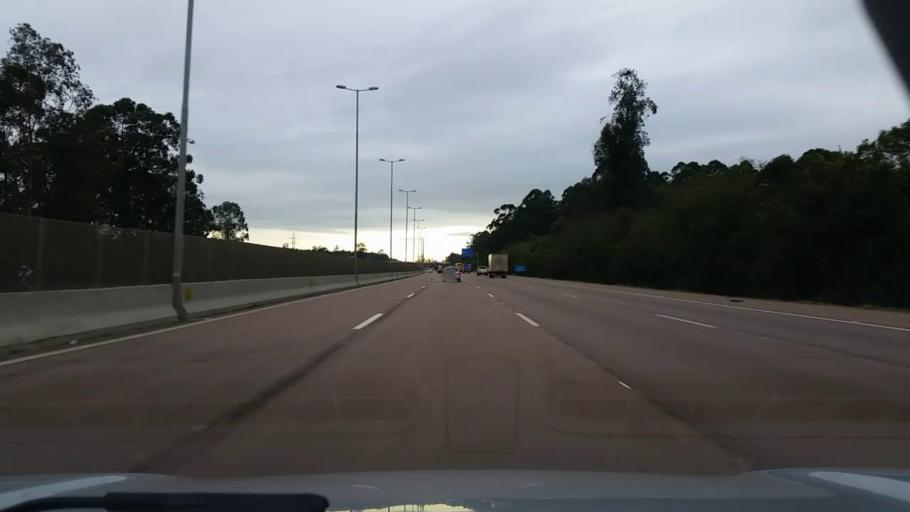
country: BR
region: Rio Grande do Sul
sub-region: Gravatai
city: Gravatai
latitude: -29.9538
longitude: -51.0420
